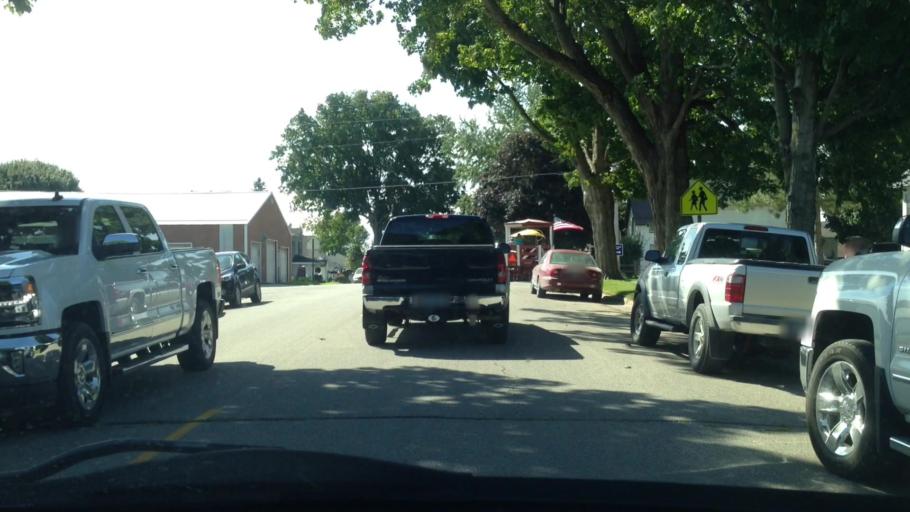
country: US
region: Minnesota
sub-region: Houston County
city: Spring Grove
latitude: 43.5210
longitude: -91.7711
